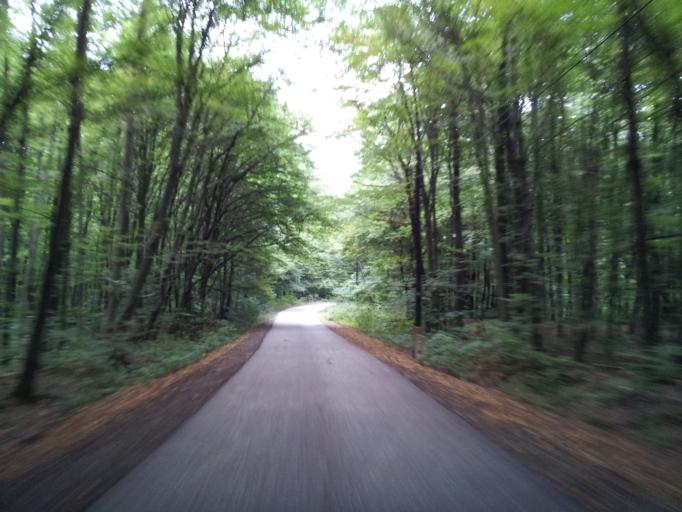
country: HU
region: Pest
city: Kismaros
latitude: 47.8849
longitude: 18.9490
